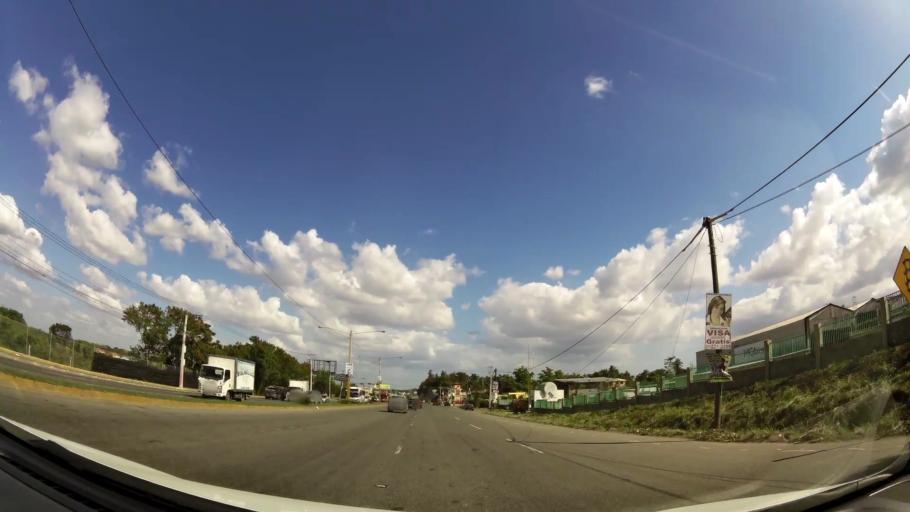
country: DO
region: Santo Domingo
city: Santo Domingo Oeste
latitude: 18.5464
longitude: -70.0403
